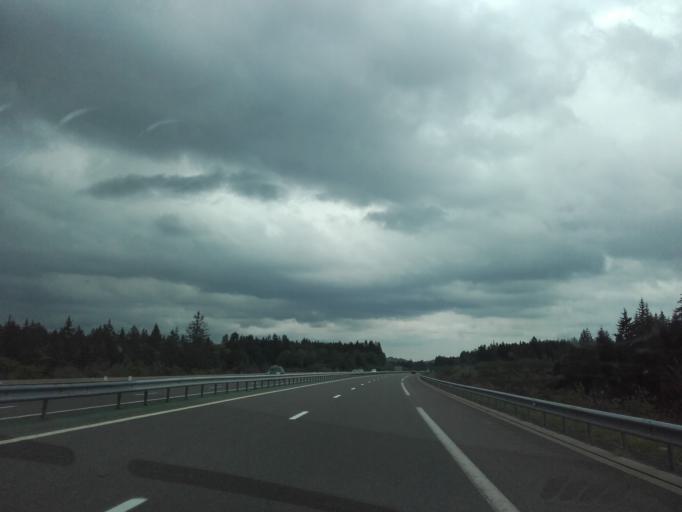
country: FR
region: Auvergne
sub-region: Departement du Puy-de-Dome
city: Gelles
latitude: 45.7492
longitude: 2.7171
